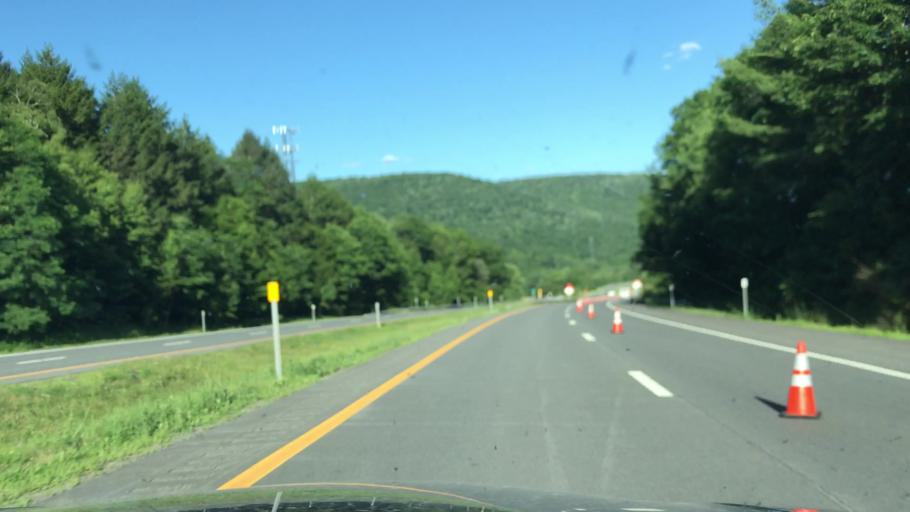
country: US
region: New York
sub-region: Delaware County
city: Walton
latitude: 41.9849
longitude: -75.0698
